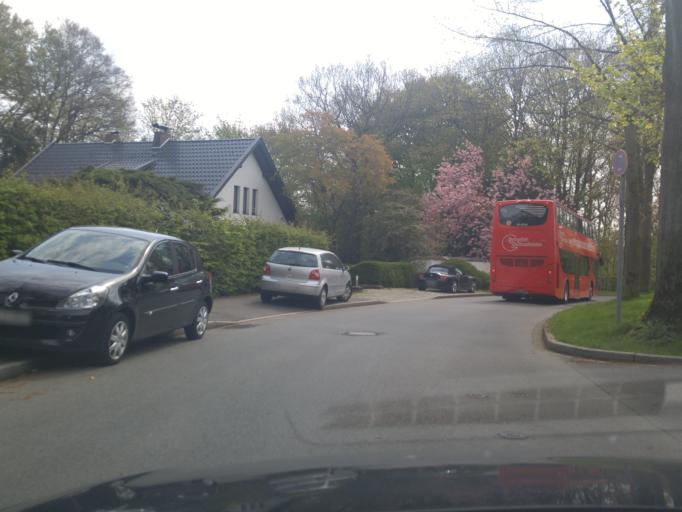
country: DE
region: North Rhine-Westphalia
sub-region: Regierungsbezirk Dusseldorf
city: Essen
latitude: 51.4146
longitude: 7.0060
